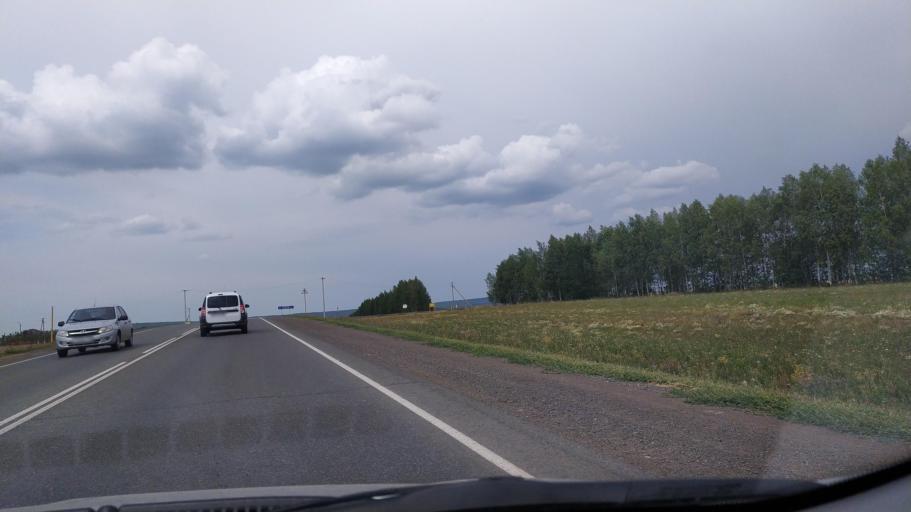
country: RU
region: Tatarstan
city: Al'met'yevsk
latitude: 54.9013
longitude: 52.2152
